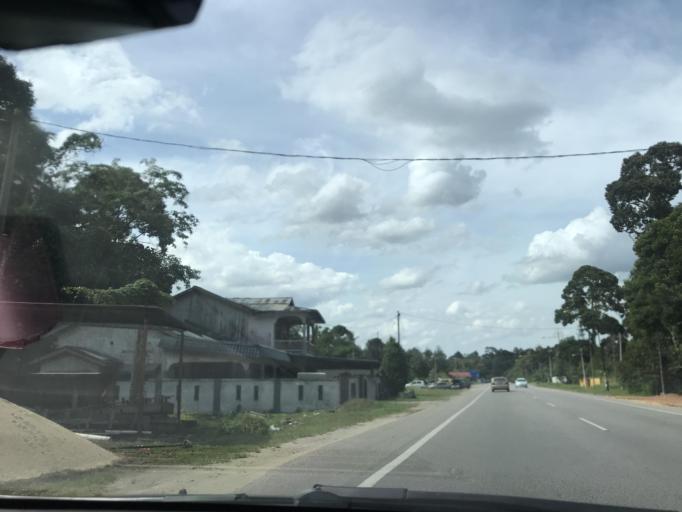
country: MY
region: Kelantan
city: Pulai Chondong
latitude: 5.8729
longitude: 102.1720
